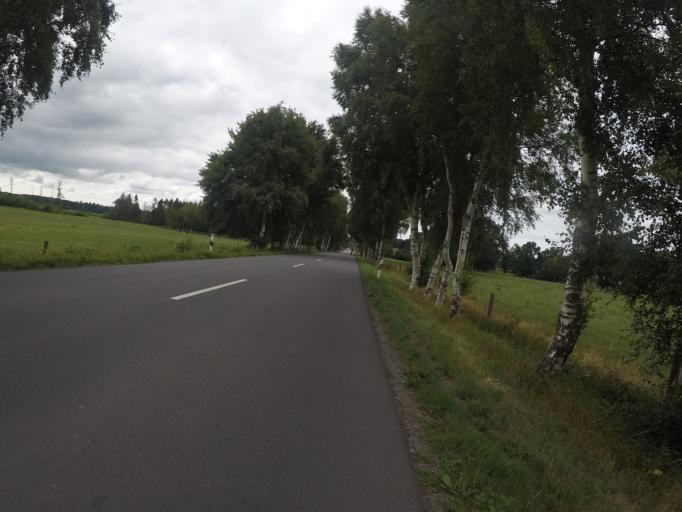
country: DE
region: Lower Saxony
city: Wingst
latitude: 53.7077
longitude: 9.0700
